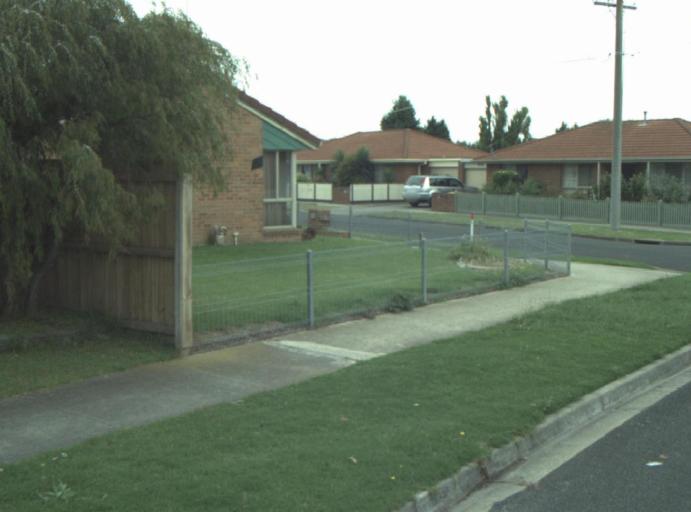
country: AU
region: Victoria
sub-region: Greater Geelong
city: Breakwater
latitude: -38.1756
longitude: 144.3967
